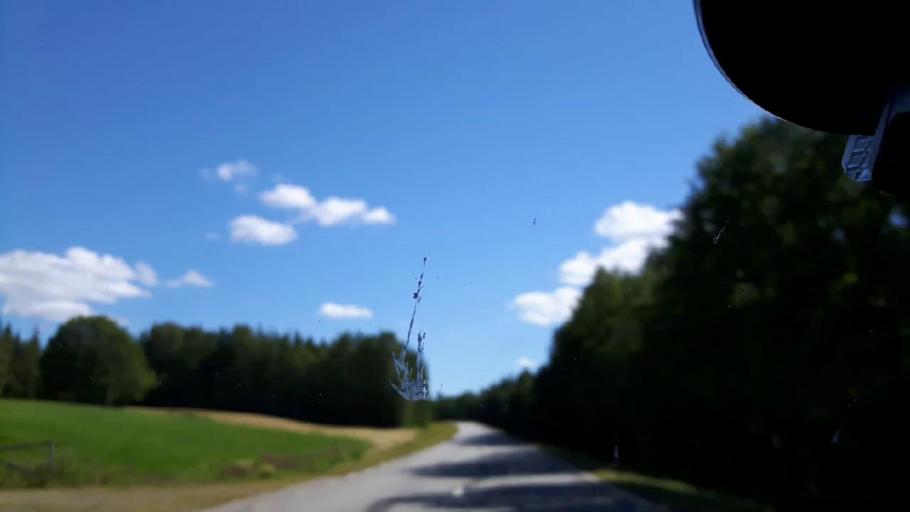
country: SE
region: Vaesternorrland
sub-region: Ange Kommun
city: Fransta
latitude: 62.7120
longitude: 16.3415
